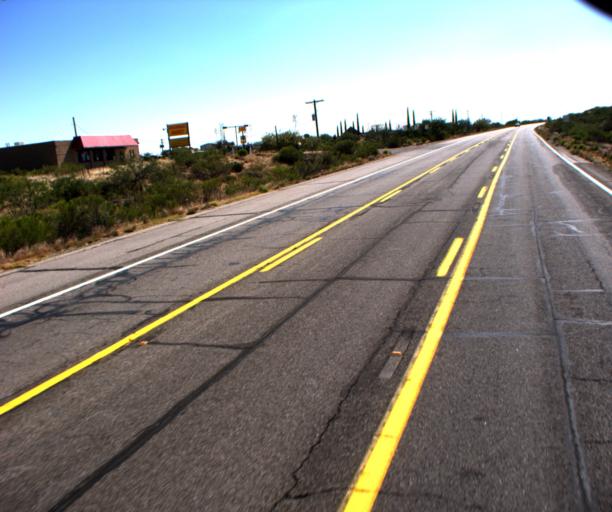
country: US
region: Arizona
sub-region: Pinal County
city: Oracle
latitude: 32.6213
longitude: -110.8000
